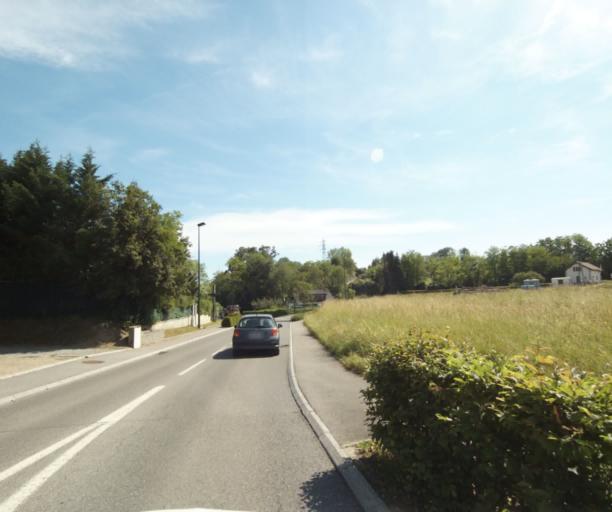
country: FR
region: Rhone-Alpes
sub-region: Departement de la Haute-Savoie
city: Margencel
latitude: 46.3419
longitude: 6.4350
